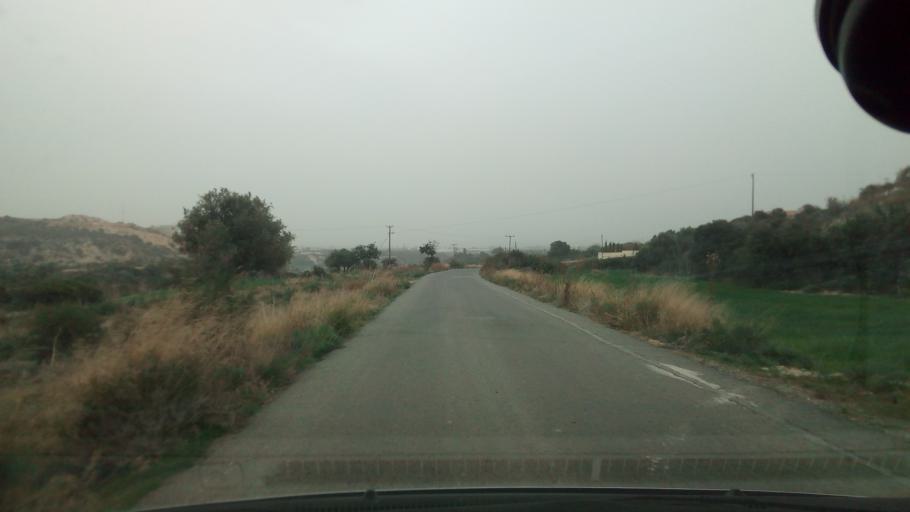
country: CY
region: Larnaka
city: Kofinou
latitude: 34.7544
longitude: 33.3660
